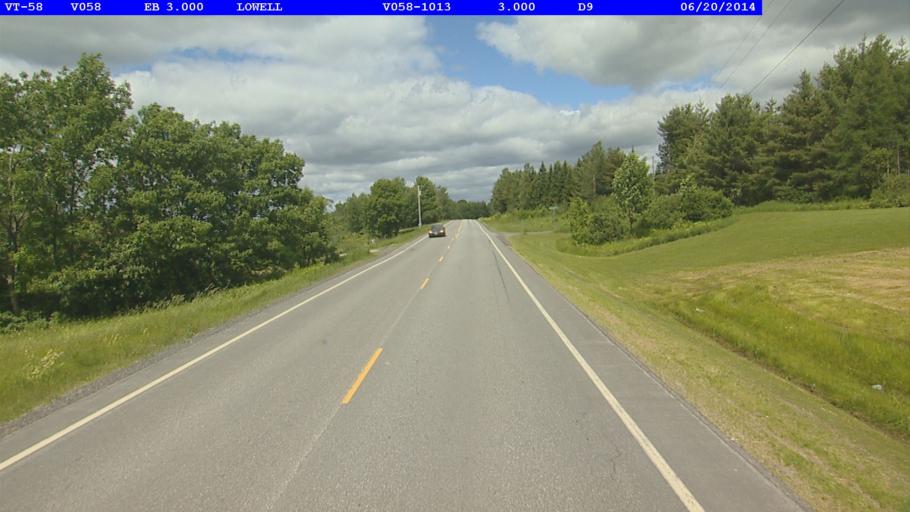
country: US
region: Vermont
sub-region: Orleans County
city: Newport
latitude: 44.8136
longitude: -72.3980
